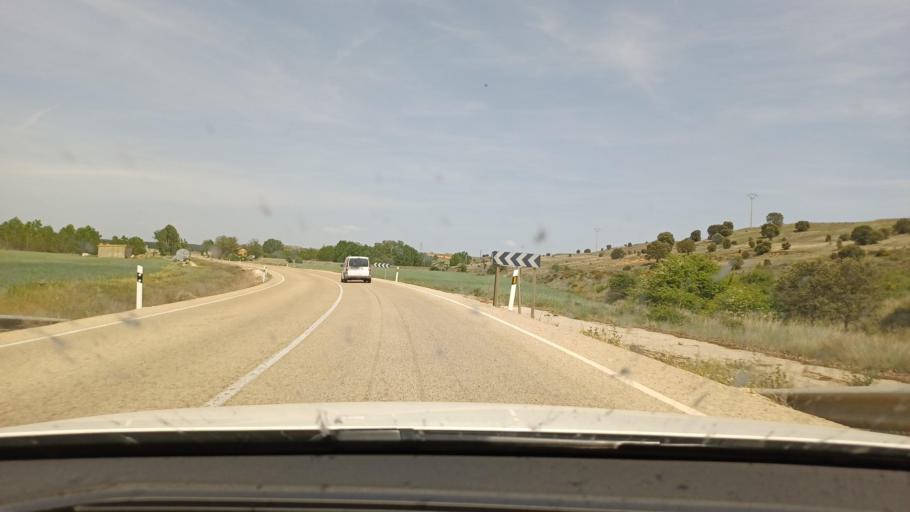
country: ES
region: Castille and Leon
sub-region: Provincia de Soria
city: Barca
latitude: 41.4654
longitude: -2.6112
